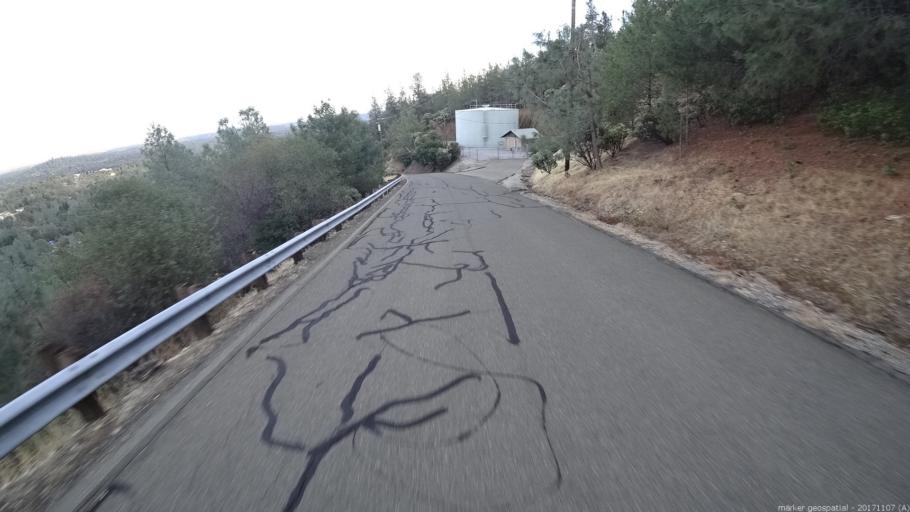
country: US
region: California
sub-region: Shasta County
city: Shasta
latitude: 40.5403
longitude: -122.4959
